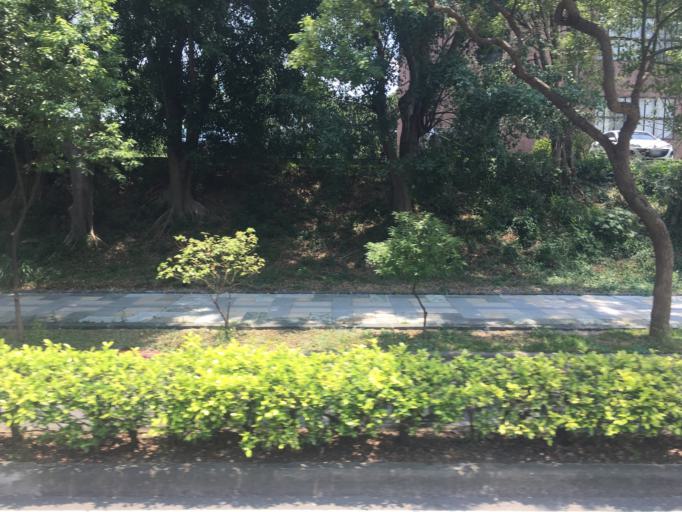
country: TW
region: Taiwan
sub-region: Hsinchu
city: Hsinchu
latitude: 24.7760
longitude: 121.0118
